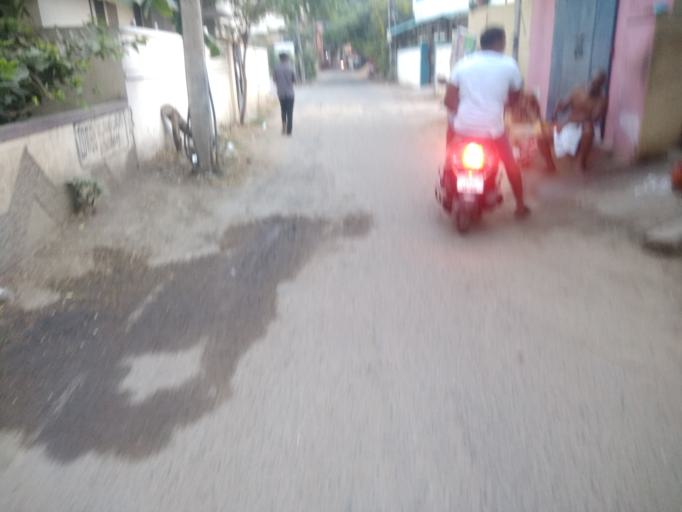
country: IN
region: Tamil Nadu
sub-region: Kancheepuram
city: Madipakkam
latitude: 12.9770
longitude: 80.2191
